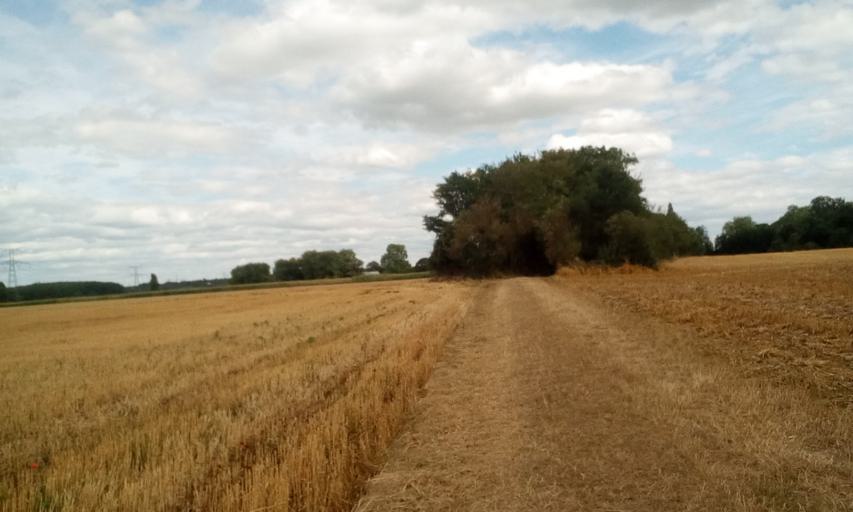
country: FR
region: Lower Normandy
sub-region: Departement du Calvados
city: Bellengreville
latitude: 49.1310
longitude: -0.2012
